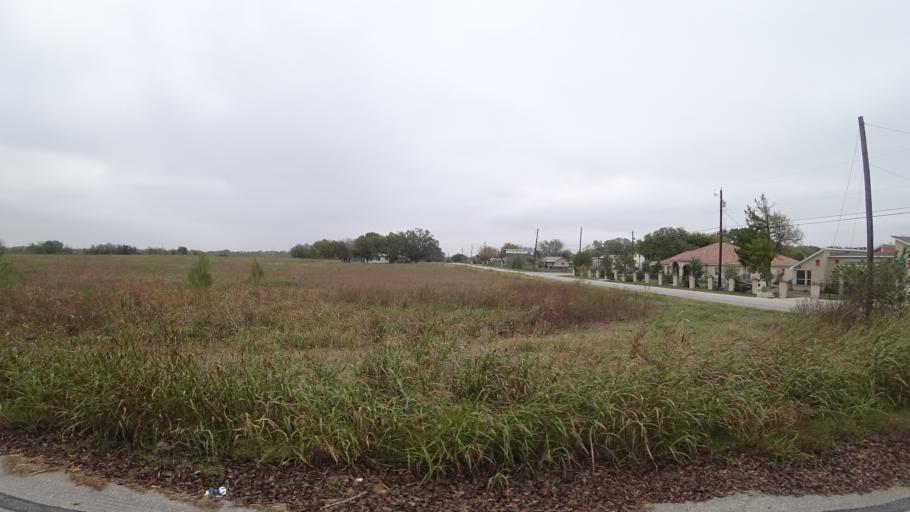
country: US
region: Texas
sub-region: Travis County
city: Pflugerville
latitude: 30.3737
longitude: -97.6245
